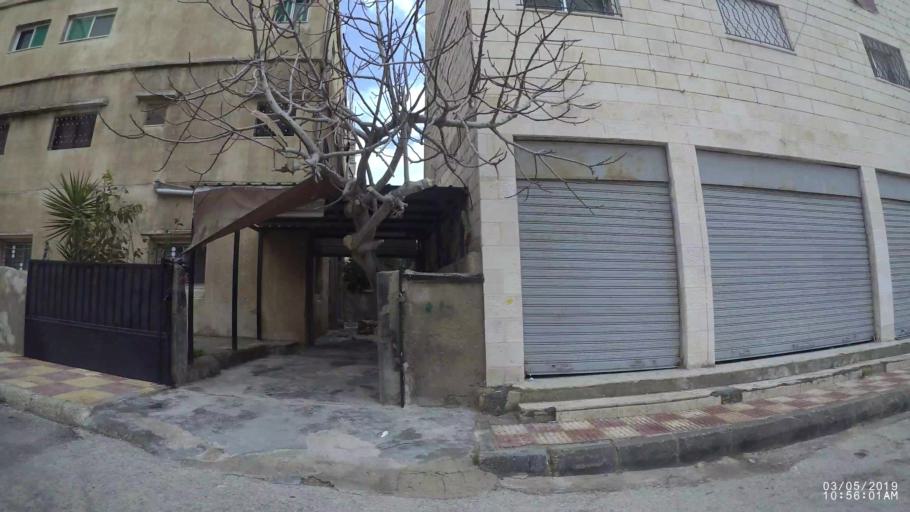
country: JO
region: Amman
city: Amman
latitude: 31.9851
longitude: 35.9217
